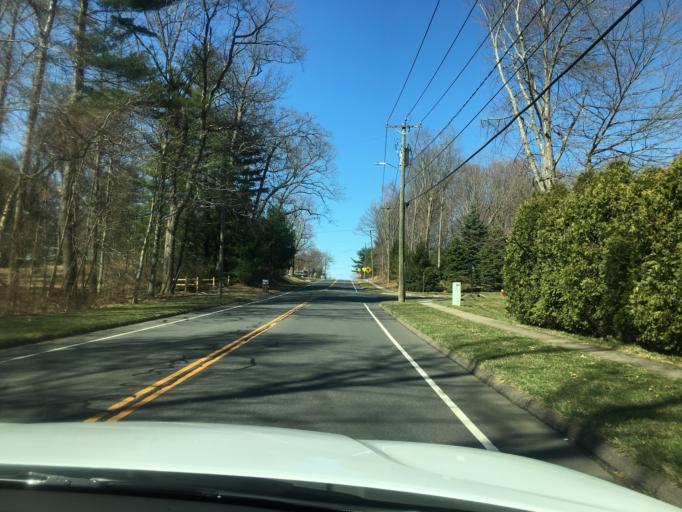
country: US
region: Connecticut
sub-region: Hartford County
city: East Hartford
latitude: 41.8052
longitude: -72.5913
